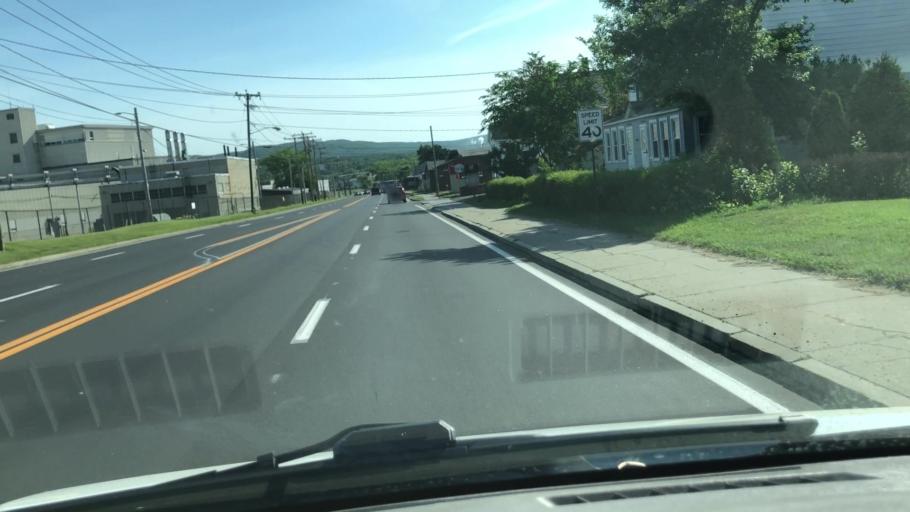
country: US
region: Massachusetts
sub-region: Berkshire County
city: Pittsfield
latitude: 42.4565
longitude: -73.2130
